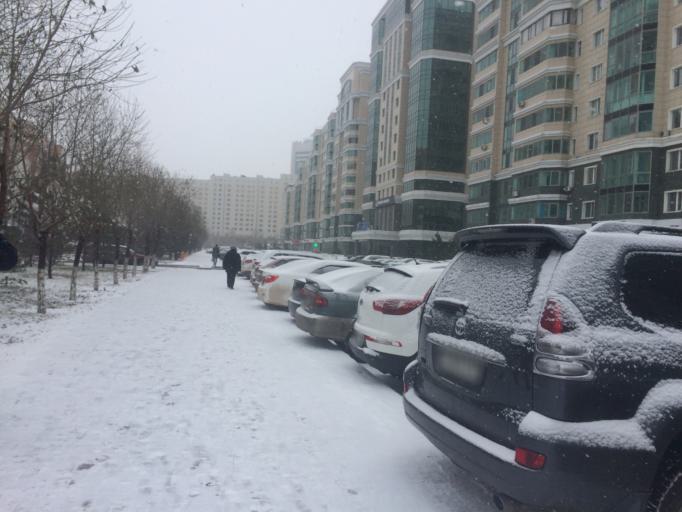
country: KZ
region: Astana Qalasy
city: Astana
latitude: 51.1299
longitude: 71.4345
